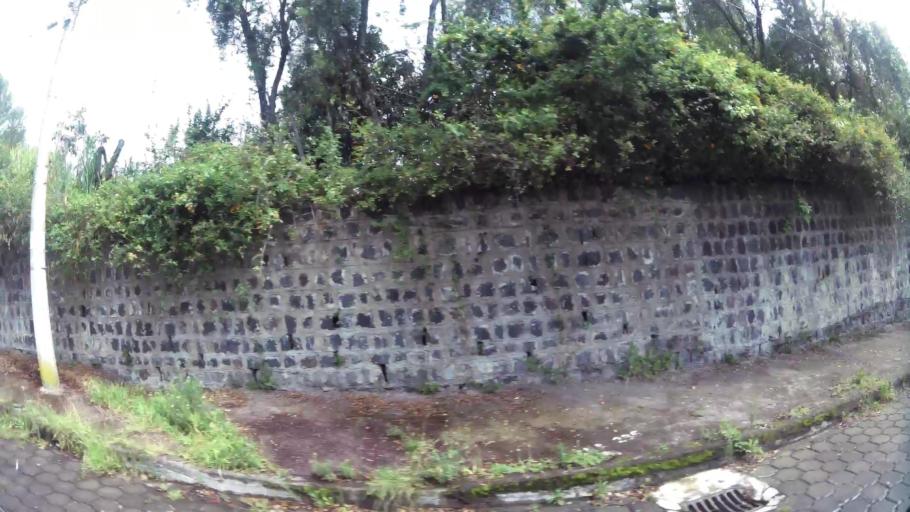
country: EC
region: Pichincha
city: Sangolqui
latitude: -0.3068
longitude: -78.4204
